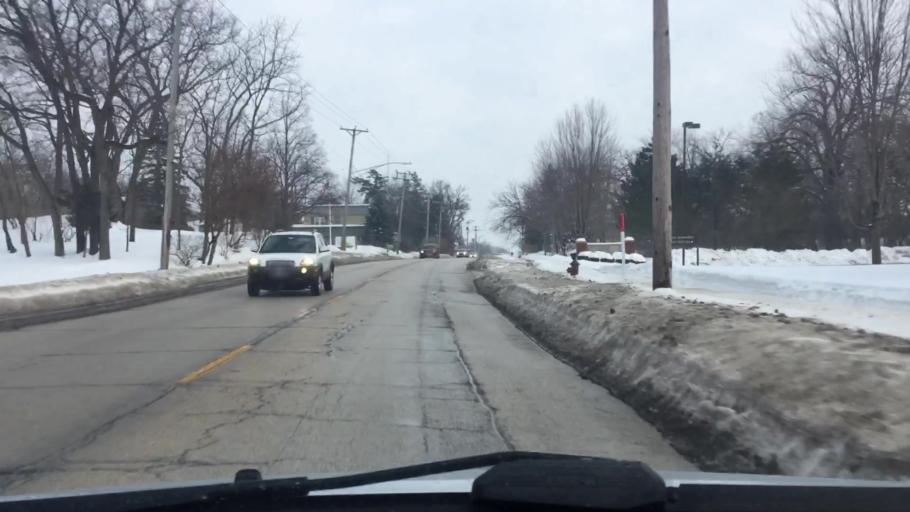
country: US
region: Illinois
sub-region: McHenry County
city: Woodstock
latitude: 42.3077
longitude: -88.4378
